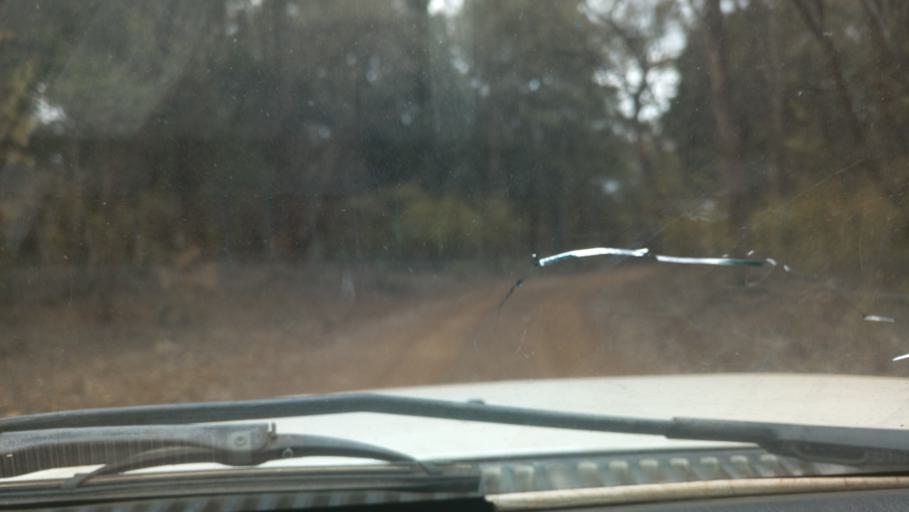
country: KE
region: Nairobi Area
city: Nairobi
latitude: -1.3643
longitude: 36.7723
